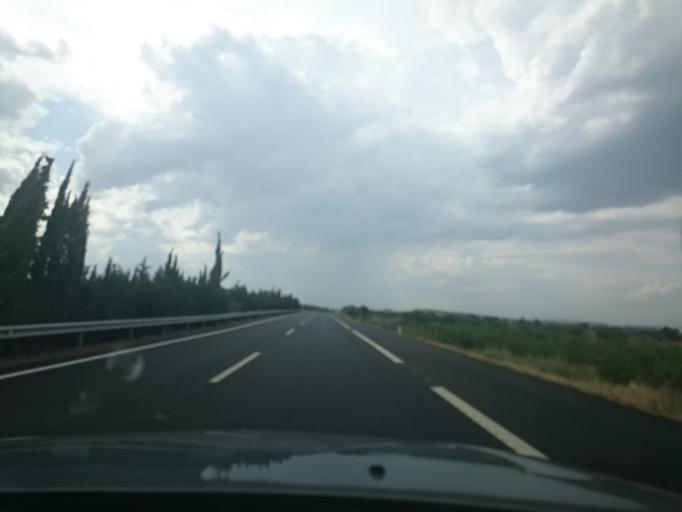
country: ES
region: La Rioja
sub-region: Provincia de La Rioja
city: Aldeanueva de Ebro
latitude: 42.2498
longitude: -1.9088
